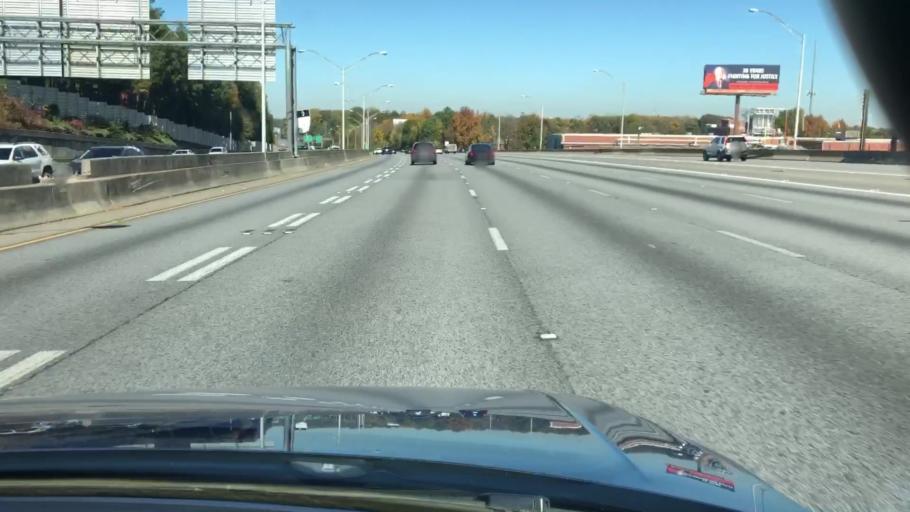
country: US
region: Georgia
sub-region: Fulton County
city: Hapeville
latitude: 33.6591
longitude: -84.3946
